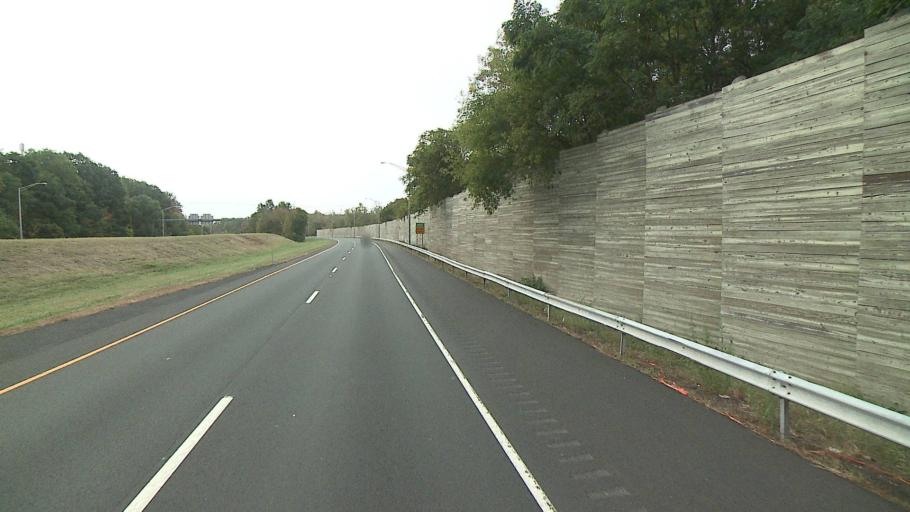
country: US
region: Connecticut
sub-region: Hartford County
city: West Hartford
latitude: 41.7194
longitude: -72.7710
